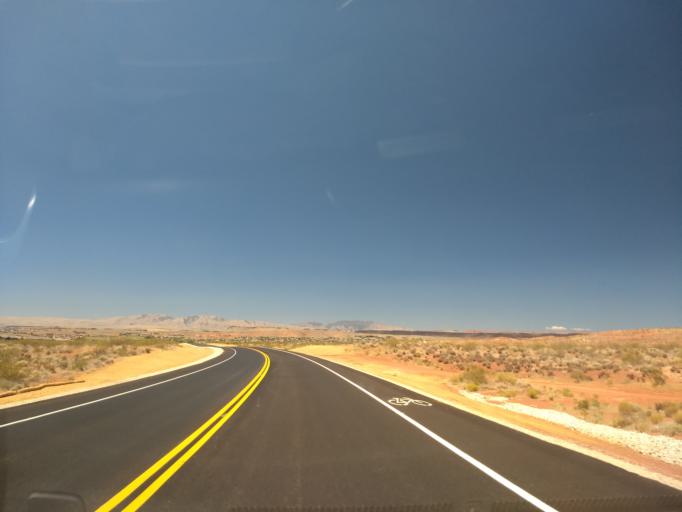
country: US
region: Utah
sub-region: Washington County
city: Washington
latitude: 37.1499
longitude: -113.4961
